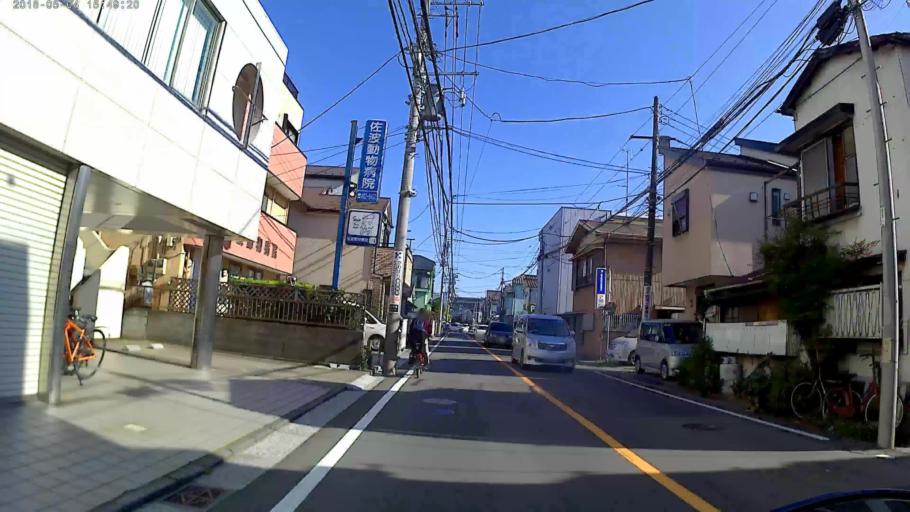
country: JP
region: Kanagawa
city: Yokohama
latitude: 35.4979
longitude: 139.6462
